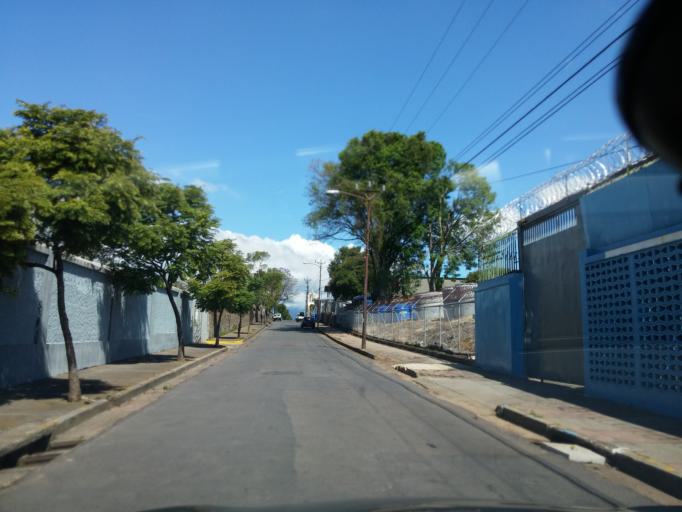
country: CR
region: San Jose
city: San Jose
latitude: 9.9271
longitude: -84.0899
